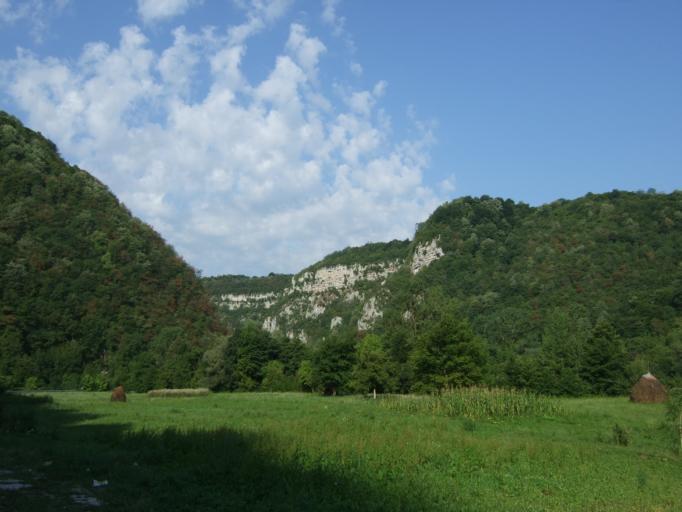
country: BA
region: Federation of Bosnia and Herzegovina
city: Bosanska Krupa
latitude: 44.8708
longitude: 16.1085
